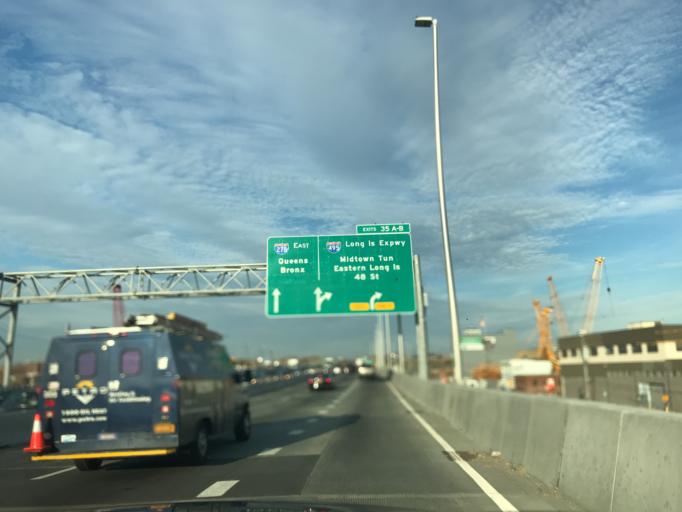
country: US
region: New York
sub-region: Queens County
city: Long Island City
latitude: 40.7304
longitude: -73.9257
